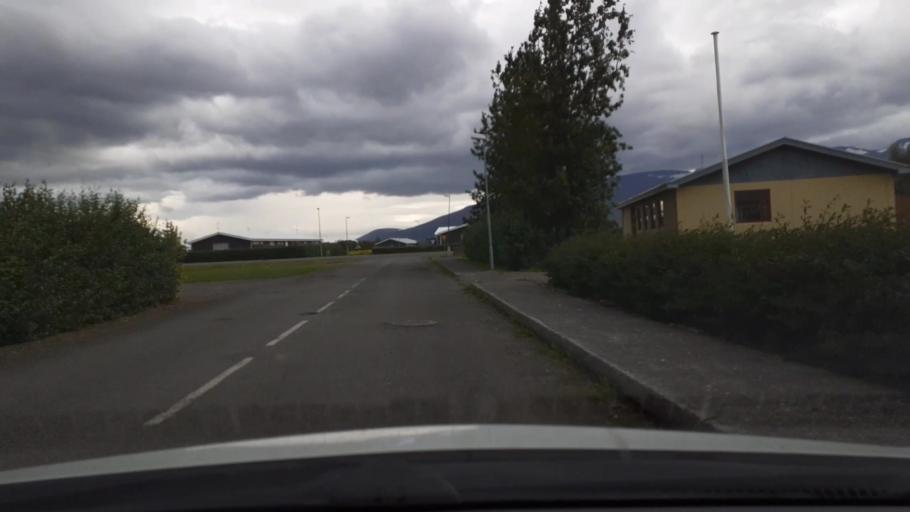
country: IS
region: West
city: Borgarnes
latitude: 64.5625
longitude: -21.7620
